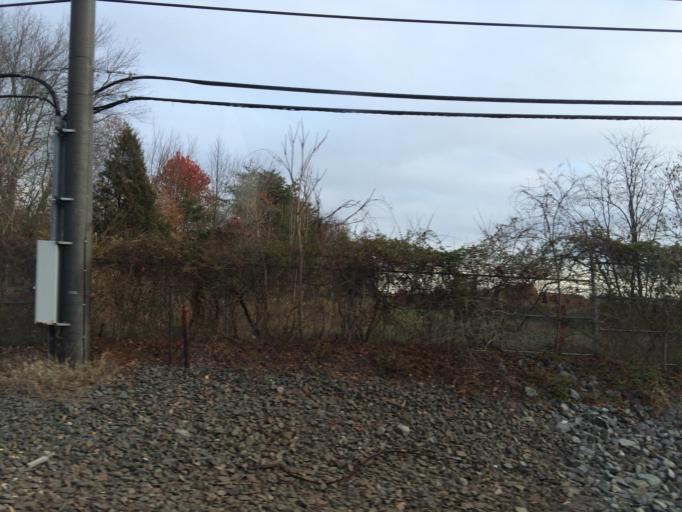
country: US
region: New Jersey
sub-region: Camden County
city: Ashland
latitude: 39.8740
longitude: -75.0142
